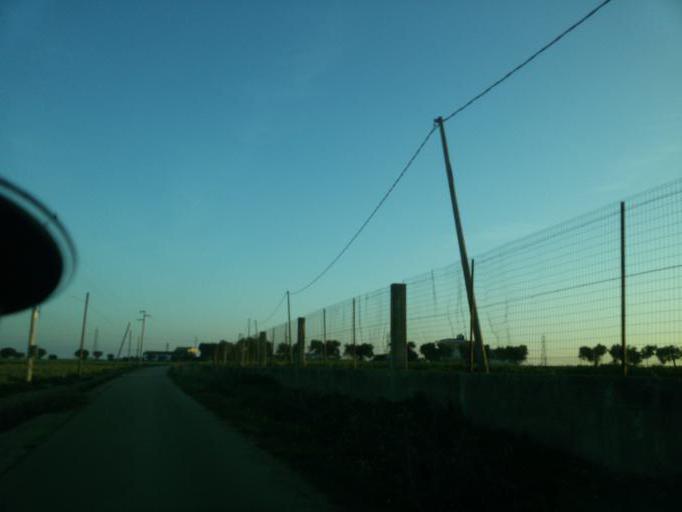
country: IT
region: Apulia
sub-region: Provincia di Brindisi
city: La Rosa
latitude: 40.6058
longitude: 17.9386
